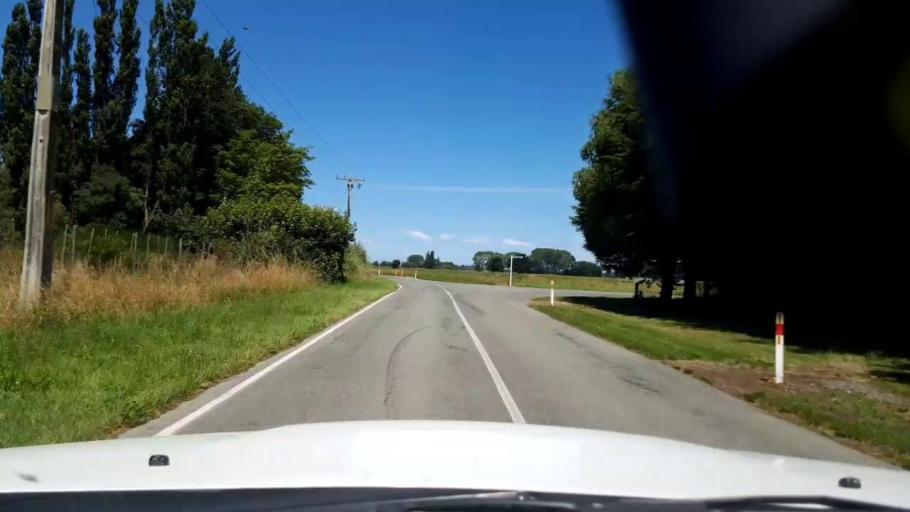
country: NZ
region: Canterbury
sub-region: Timaru District
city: Pleasant Point
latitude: -44.1647
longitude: 171.3071
